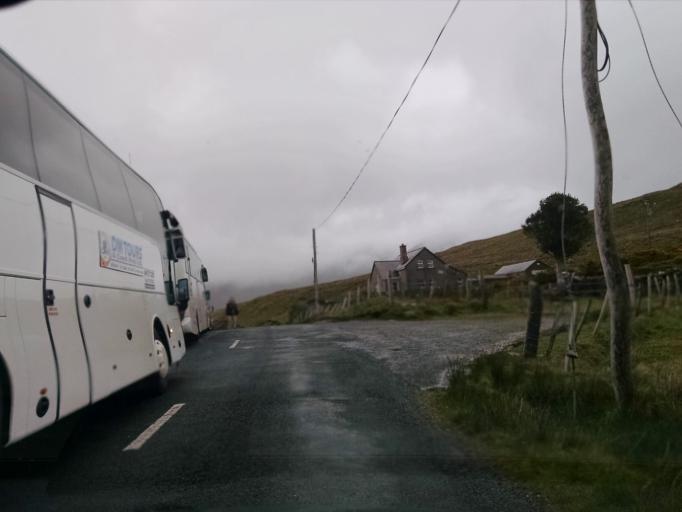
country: IE
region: Connaught
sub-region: County Galway
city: Clifden
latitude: 53.4960
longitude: -9.7352
